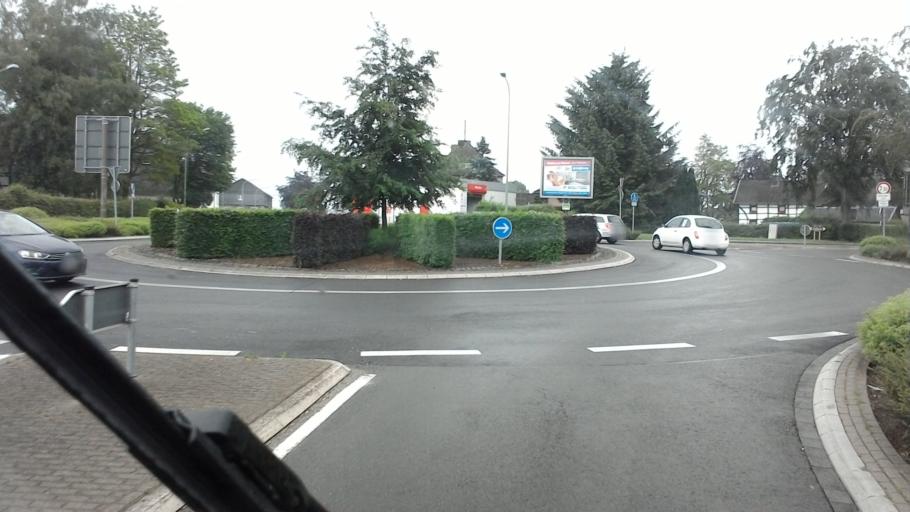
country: DE
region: North Rhine-Westphalia
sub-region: Regierungsbezirk Koln
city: Monschau
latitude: 50.5763
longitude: 6.2618
